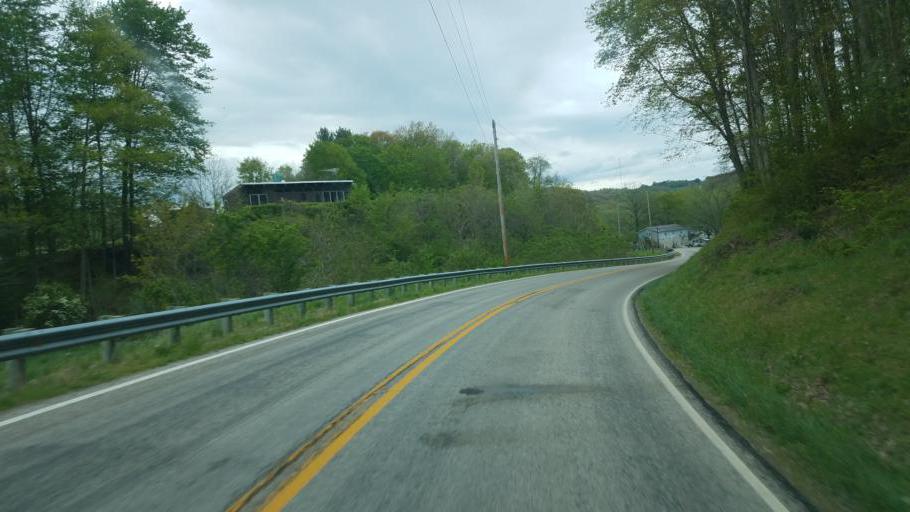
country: US
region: Ohio
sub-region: Ashland County
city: Loudonville
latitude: 40.6546
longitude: -82.3209
